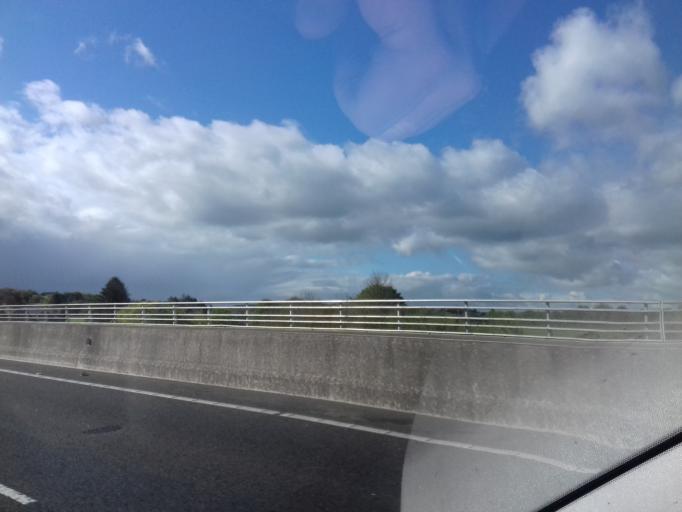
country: IE
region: Leinster
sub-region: Kilkenny
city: Mooncoin
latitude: 52.4024
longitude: -7.1862
